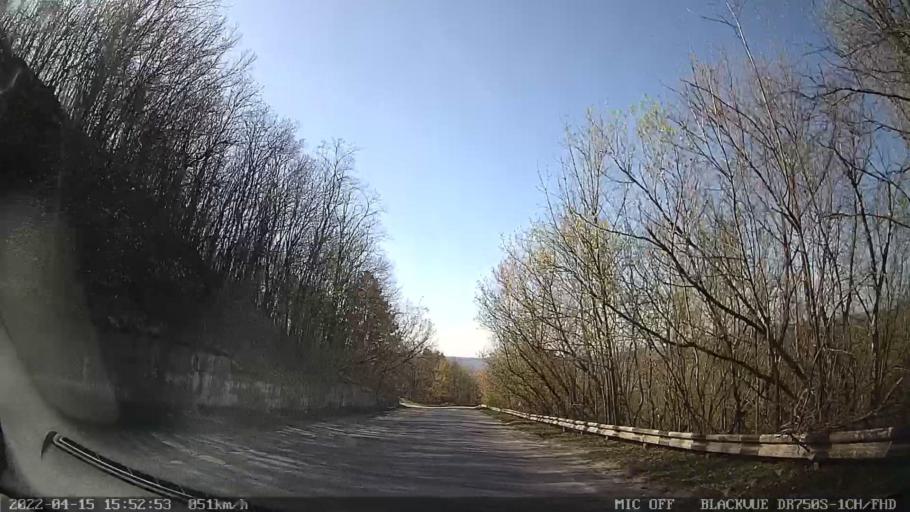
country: MD
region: Raionul Ocnita
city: Otaci
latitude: 48.3965
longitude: 27.8896
